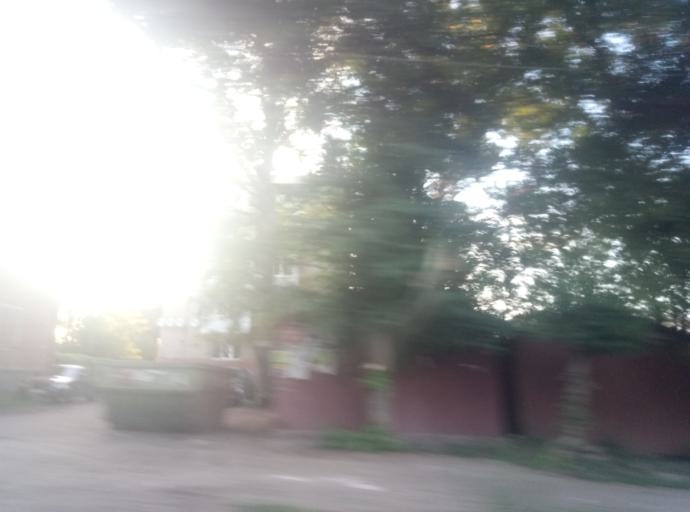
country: RU
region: Tula
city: Kireyevsk
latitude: 53.9261
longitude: 37.9287
